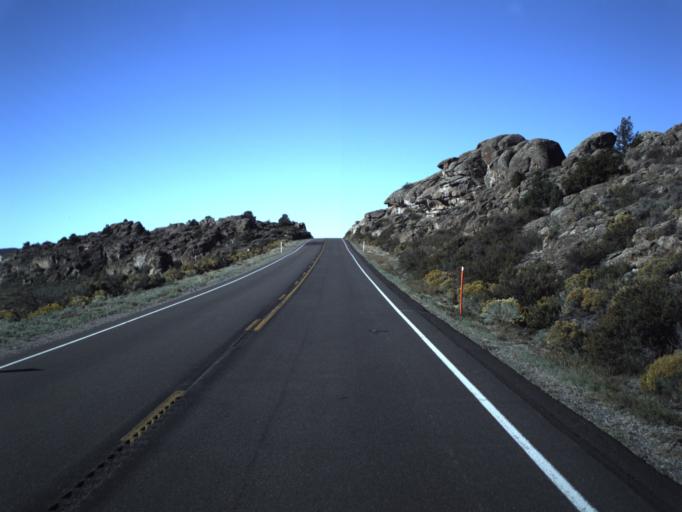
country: US
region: Utah
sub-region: Washington County
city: Enterprise
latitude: 37.7319
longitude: -114.0264
